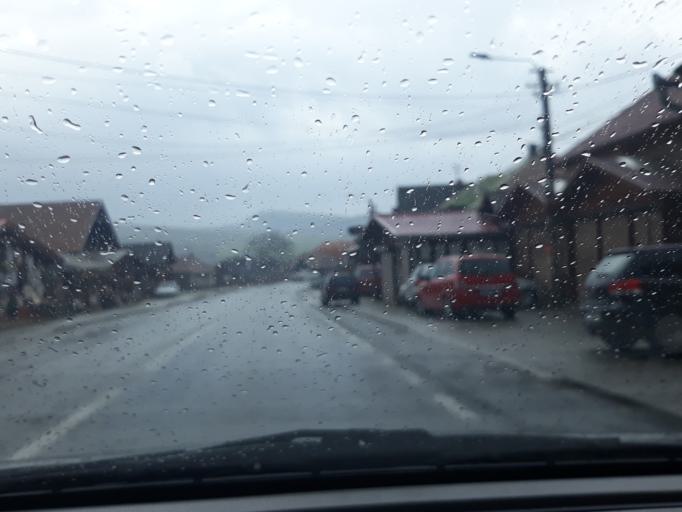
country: RO
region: Harghita
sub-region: Comuna Corund
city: Corund
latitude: 46.4737
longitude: 25.1792
